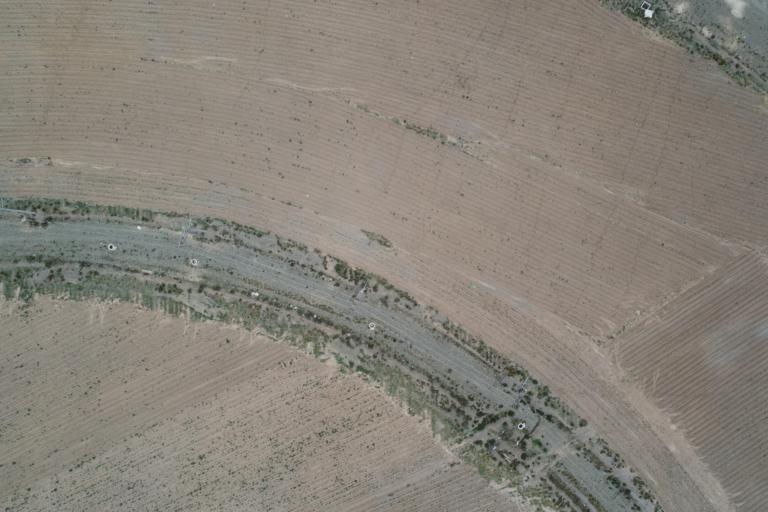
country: BO
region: La Paz
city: La Paz
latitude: -16.5203
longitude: -68.2982
